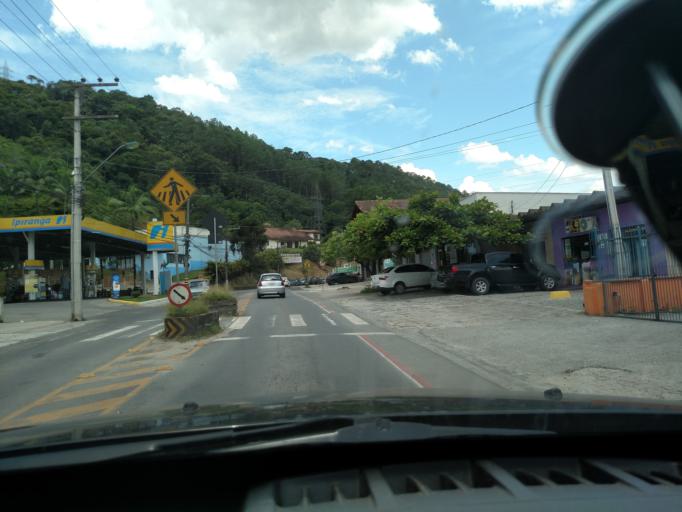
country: BR
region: Santa Catarina
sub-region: Blumenau
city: Blumenau
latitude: -26.9550
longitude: -49.0671
